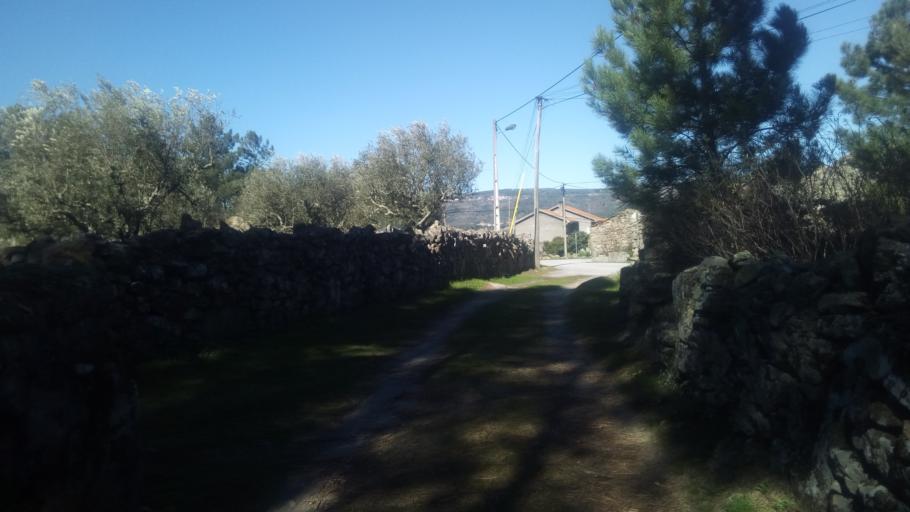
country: PT
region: Guarda
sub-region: Fornos de Algodres
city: Fornos de Algodres
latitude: 40.6045
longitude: -7.5071
